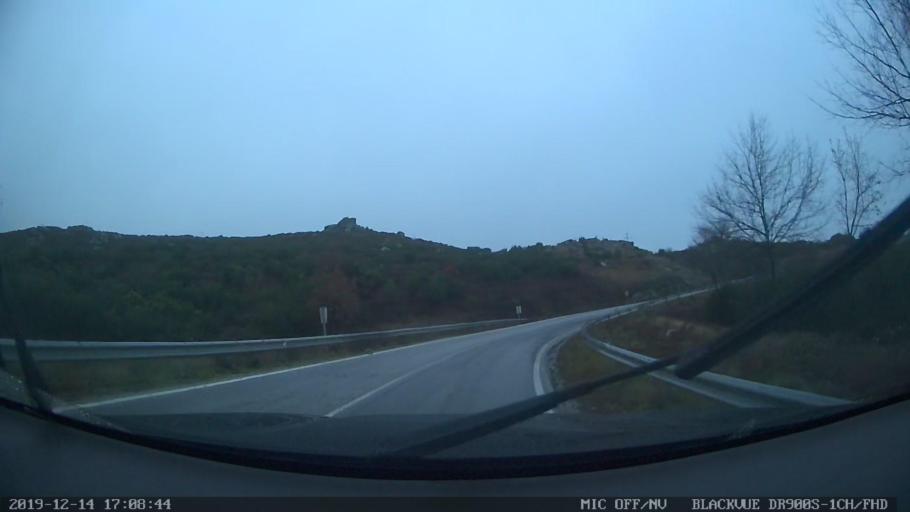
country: PT
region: Vila Real
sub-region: Vila Pouca de Aguiar
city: Vila Pouca de Aguiar
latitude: 41.4711
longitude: -7.6046
